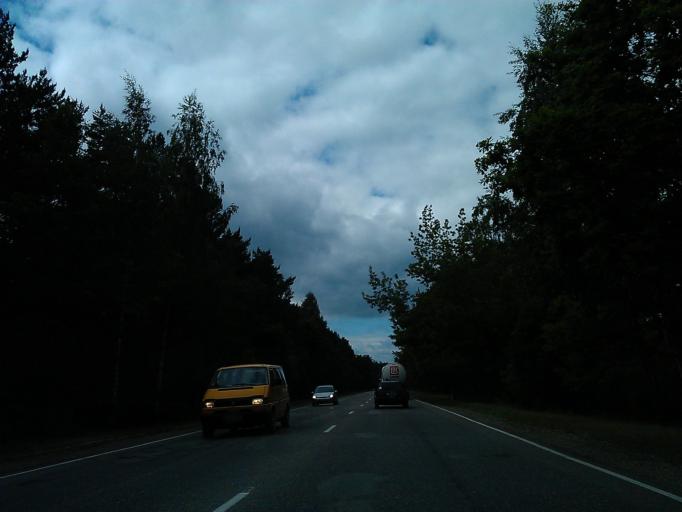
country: LV
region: Jurmala
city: Jurmala
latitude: 56.9561
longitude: 23.8270
